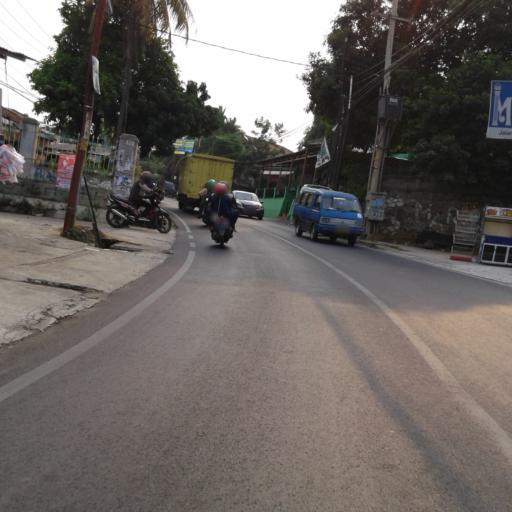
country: ID
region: West Java
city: Sawangan
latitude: -6.4036
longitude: 106.7663
